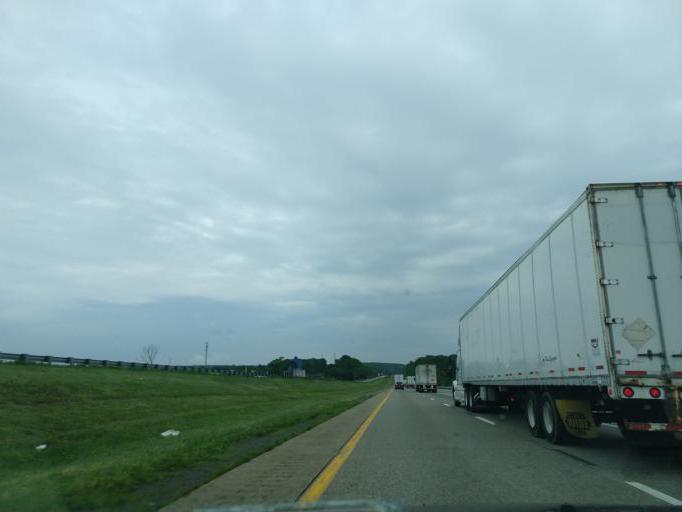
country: US
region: Pennsylvania
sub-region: Luzerne County
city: Conyngham
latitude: 40.9779
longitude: -76.0350
